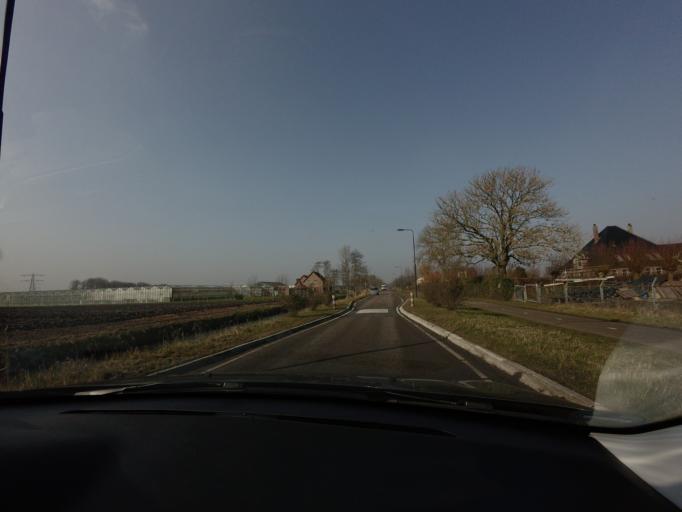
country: NL
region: North Holland
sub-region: Gemeente Heerhugowaard
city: Heerhugowaard
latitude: 52.6402
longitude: 4.8653
